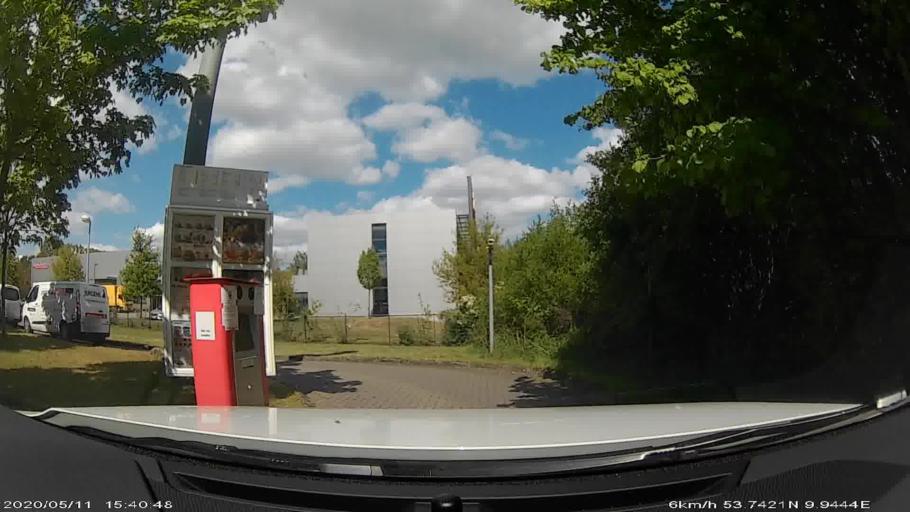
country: DE
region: Schleswig-Holstein
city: Ellerau
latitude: 53.7426
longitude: 9.9446
